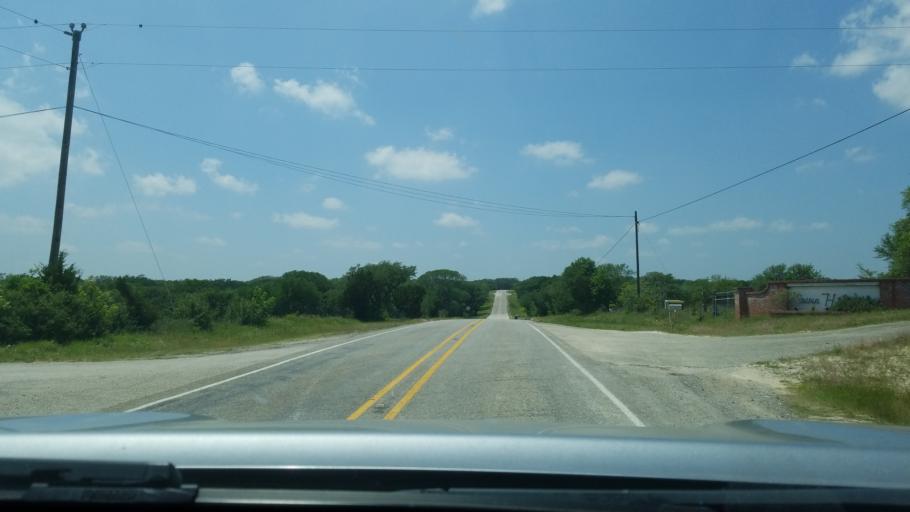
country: US
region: Texas
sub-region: Hays County
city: Woodcreek
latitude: 30.0988
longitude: -98.2513
